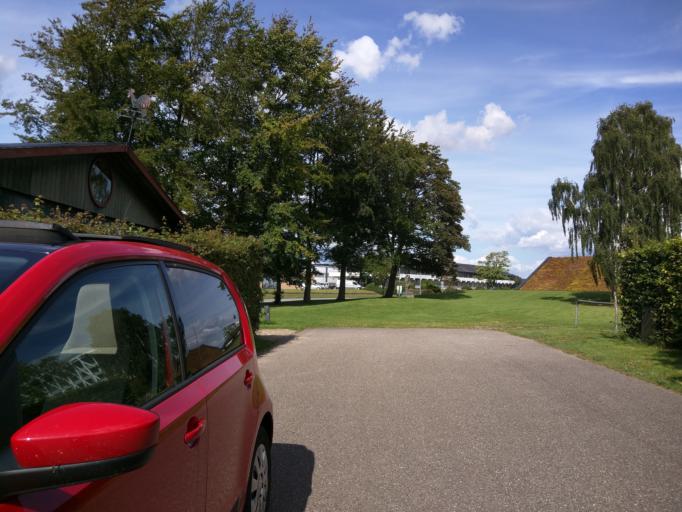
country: DK
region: Central Jutland
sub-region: Viborg Kommune
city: Viborg
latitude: 56.4577
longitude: 9.3965
